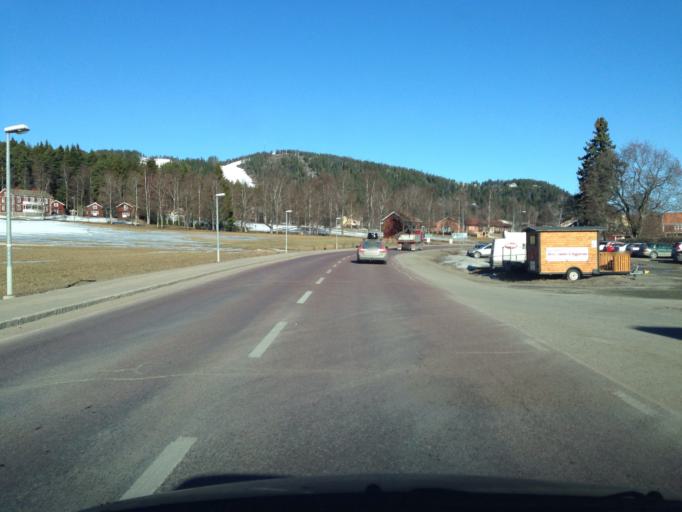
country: SE
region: Gaevleborg
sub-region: Ljusdals Kommun
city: Jaervsoe
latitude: 61.7055
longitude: 16.1637
